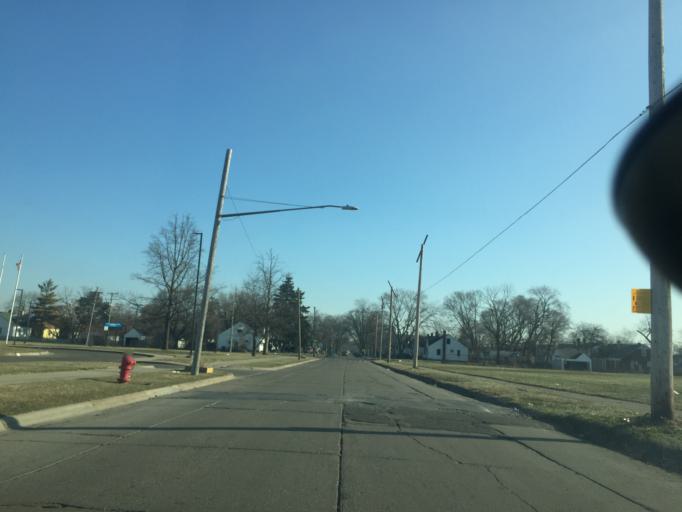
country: US
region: Michigan
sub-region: Macomb County
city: Eastpointe
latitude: 42.4364
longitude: -82.9621
